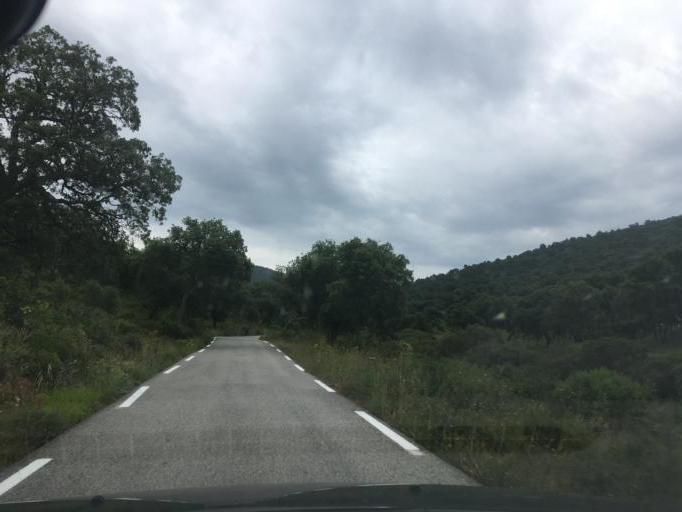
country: FR
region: Provence-Alpes-Cote d'Azur
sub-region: Departement du Var
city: Pierrefeu-du-Var
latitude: 43.2302
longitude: 6.2136
